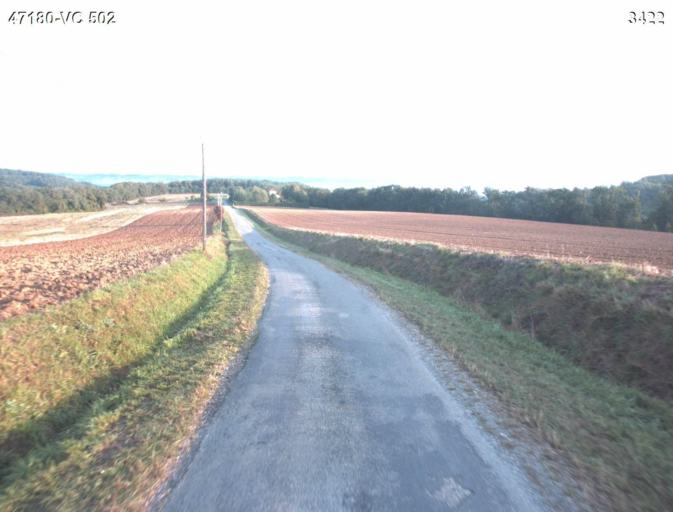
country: FR
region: Aquitaine
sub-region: Departement du Lot-et-Garonne
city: Sainte-Colombe-en-Bruilhois
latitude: 44.1873
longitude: 0.4823
